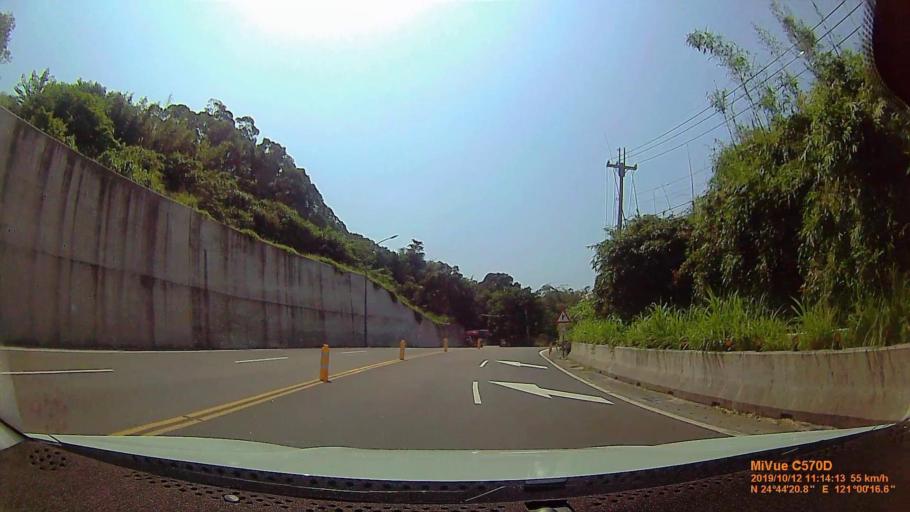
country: TW
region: Taiwan
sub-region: Hsinchu
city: Hsinchu
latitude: 24.7390
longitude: 121.0045
